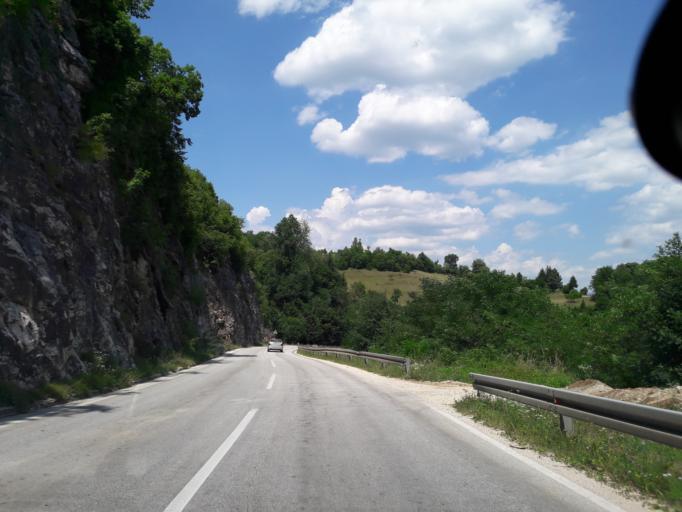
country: BA
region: Republika Srpska
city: Mrkonjic Grad
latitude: 44.4172
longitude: 17.0992
